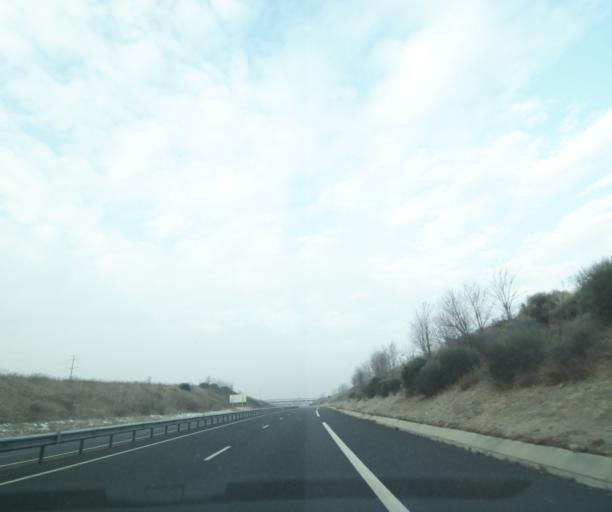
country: FR
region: Rhone-Alpes
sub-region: Departement de l'Ain
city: Mionnay
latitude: 45.8578
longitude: 4.9311
